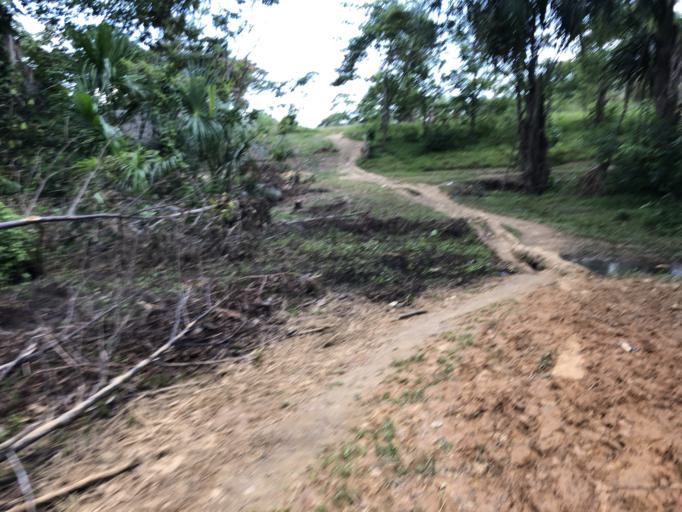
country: PE
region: Loreto
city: Puerto Galilea
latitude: -4.0549
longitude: -77.7615
